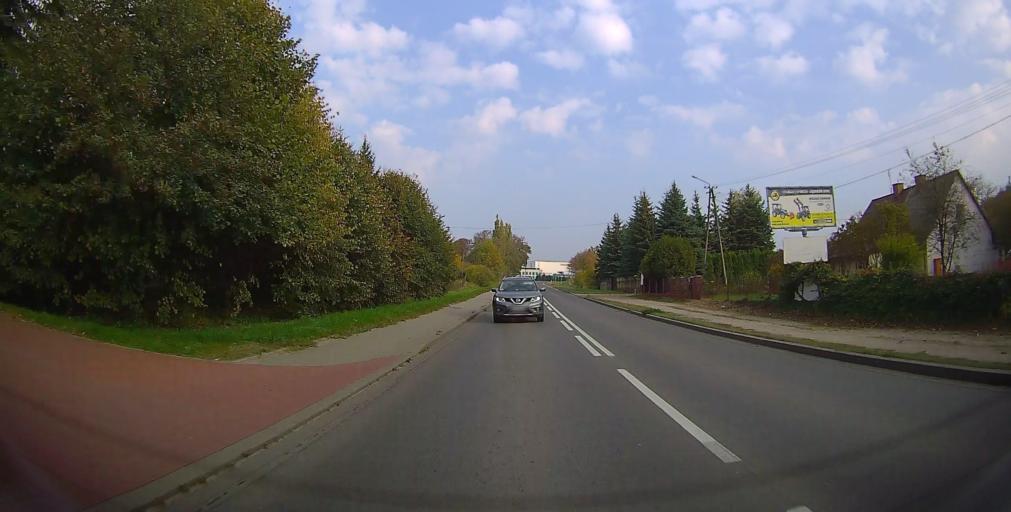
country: PL
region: Masovian Voivodeship
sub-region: Powiat grojecki
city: Belsk Duzy
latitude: 51.8146
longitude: 20.7970
